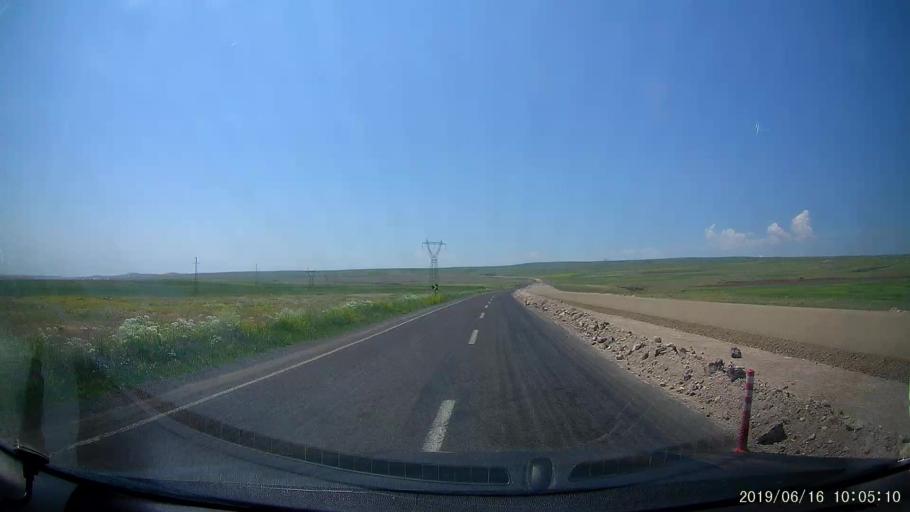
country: TR
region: Kars
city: Digor
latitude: 40.2742
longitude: 43.5374
